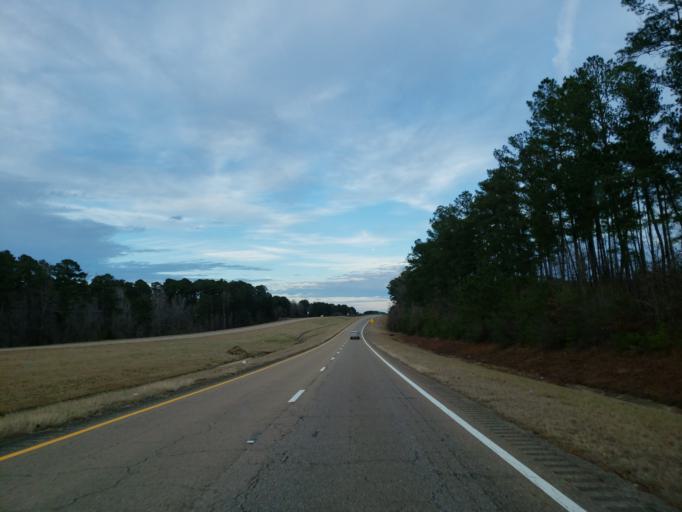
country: US
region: Mississippi
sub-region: Lauderdale County
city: Meridian Station
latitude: 32.4865
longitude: -88.5900
